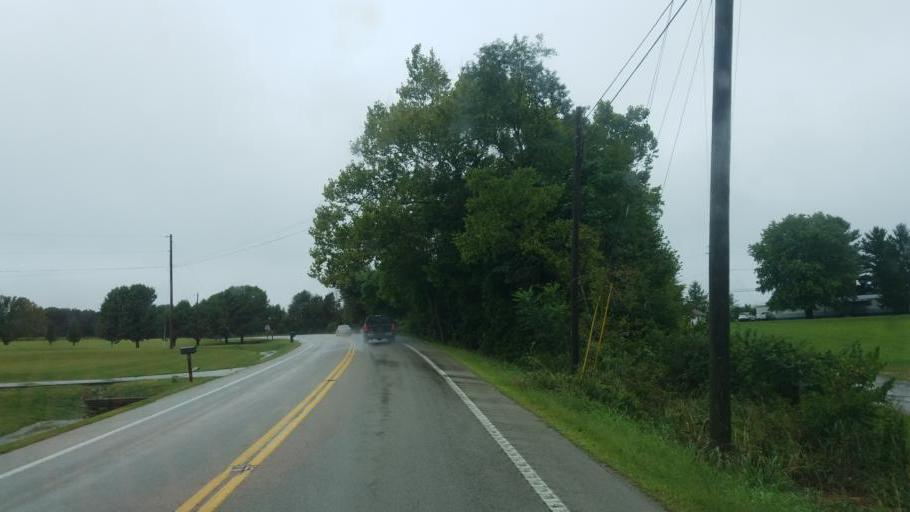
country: US
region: Ohio
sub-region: Adams County
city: West Union
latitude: 38.8004
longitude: -83.4718
